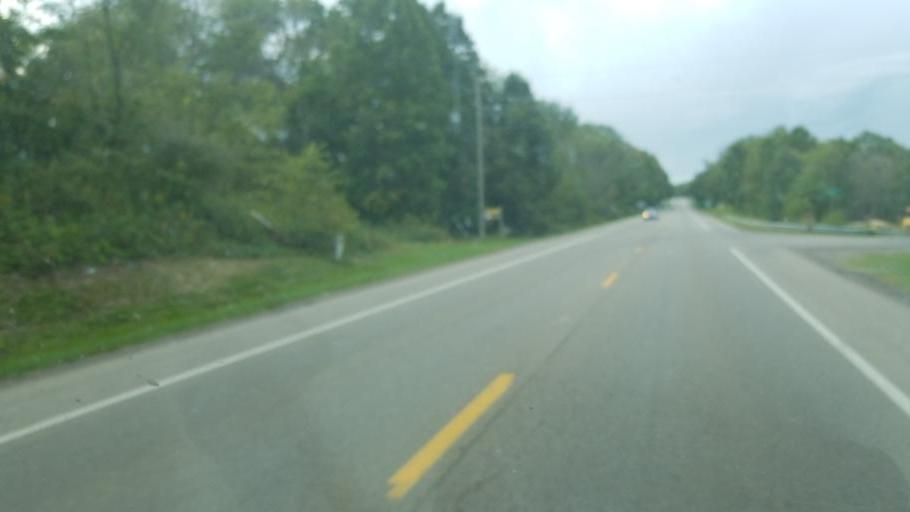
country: US
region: Ohio
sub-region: Tuscarawas County
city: Sugarcreek
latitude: 40.5162
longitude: -81.6645
